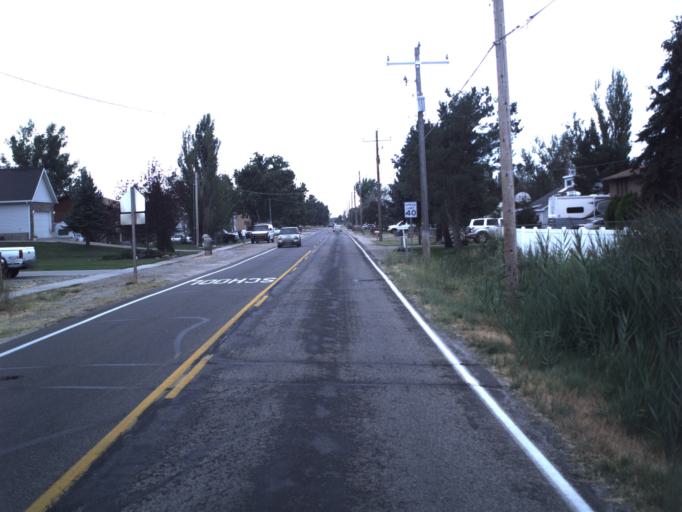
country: US
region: Utah
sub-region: Davis County
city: West Point
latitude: 41.1170
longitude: -112.1126
